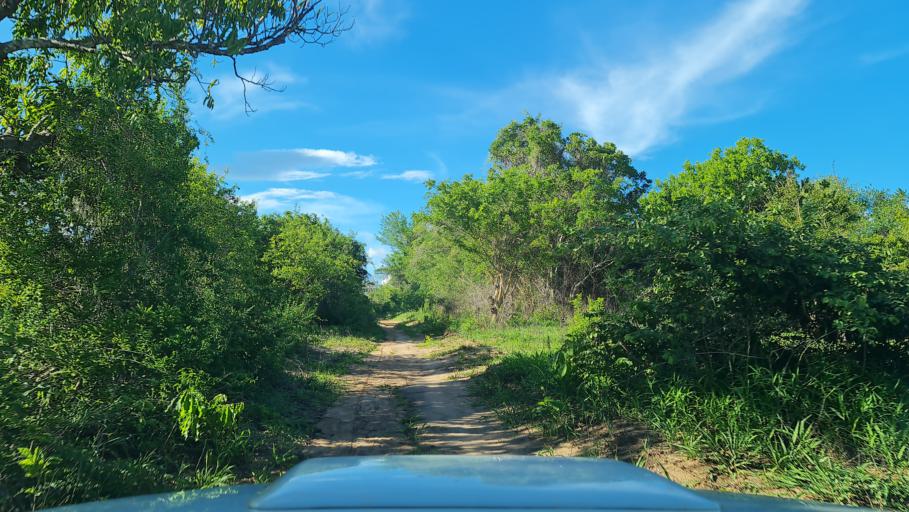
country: MZ
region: Nampula
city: Ilha de Mocambique
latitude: -15.2531
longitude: 40.1818
